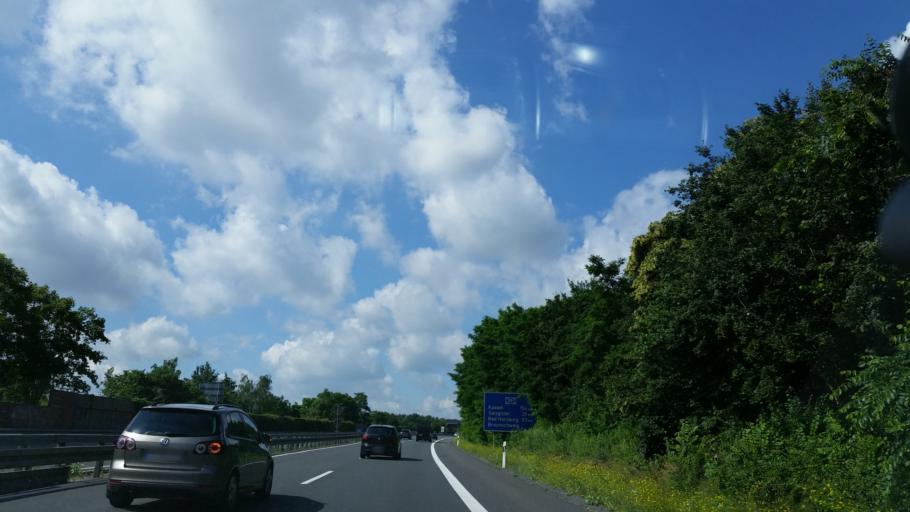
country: DE
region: Lower Saxony
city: Braunschweig
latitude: 52.2998
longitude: 10.5050
